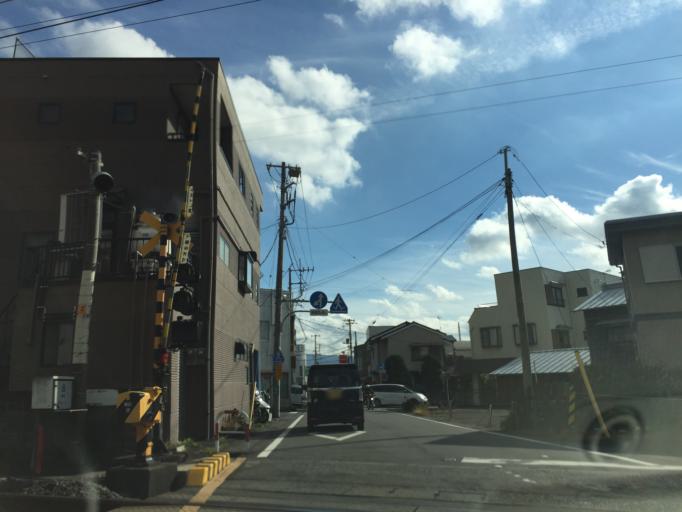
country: JP
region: Shizuoka
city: Mishima
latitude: 35.1244
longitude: 138.9045
